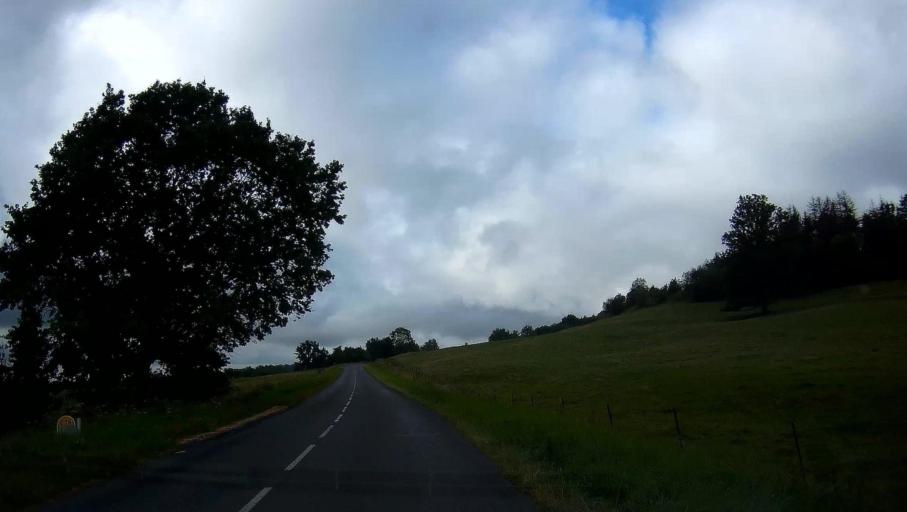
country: FR
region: Picardie
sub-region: Departement de l'Aisne
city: Rozoy-sur-Serre
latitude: 49.6761
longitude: 4.2509
